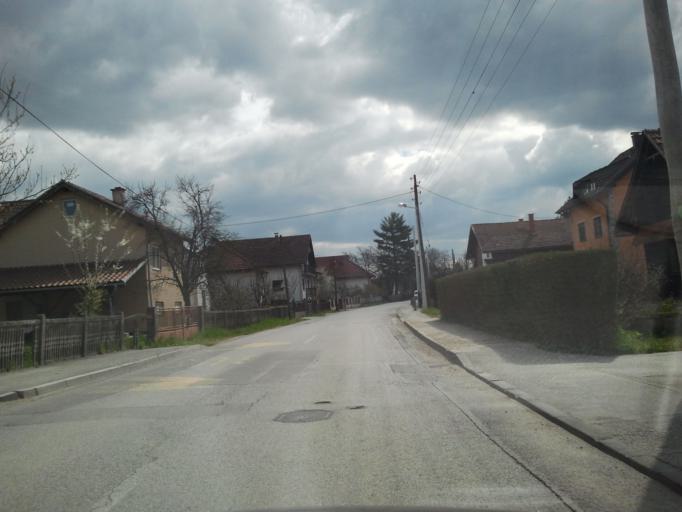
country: HR
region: Grad Zagreb
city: Brezovica
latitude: 45.7320
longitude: 15.8994
